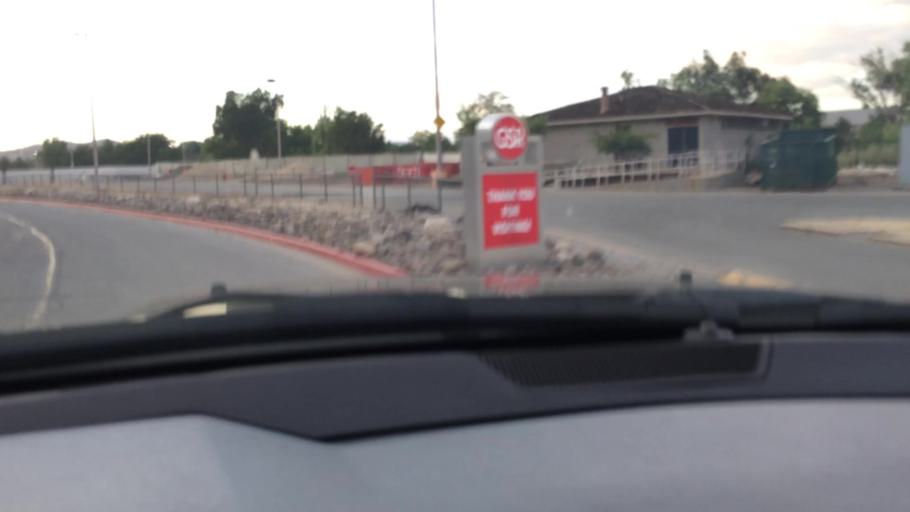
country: US
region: Nevada
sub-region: Washoe County
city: Sparks
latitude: 39.5235
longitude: -119.7768
